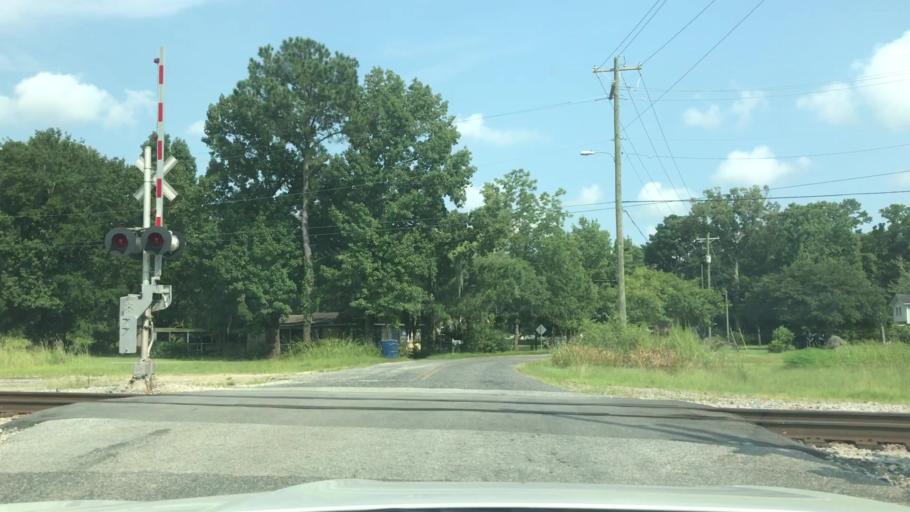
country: US
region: South Carolina
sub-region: Charleston County
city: Shell Point
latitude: 32.8153
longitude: -80.0835
